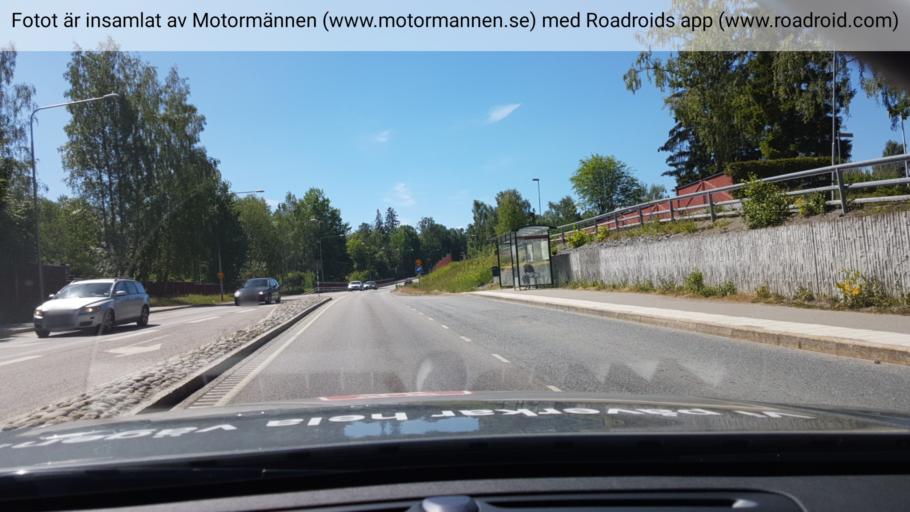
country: SE
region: Stockholm
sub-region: Tyreso Kommun
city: Bollmora
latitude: 59.2100
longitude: 18.2082
